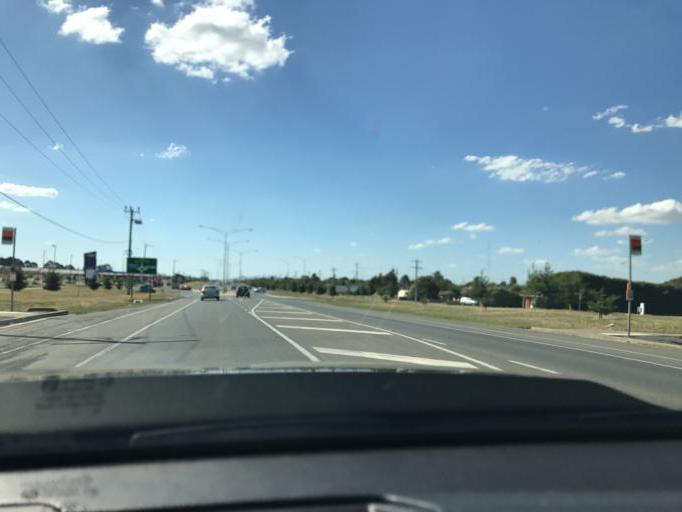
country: AU
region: Victoria
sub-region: Ballarat North
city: Newington
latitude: -37.5356
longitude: 143.8191
